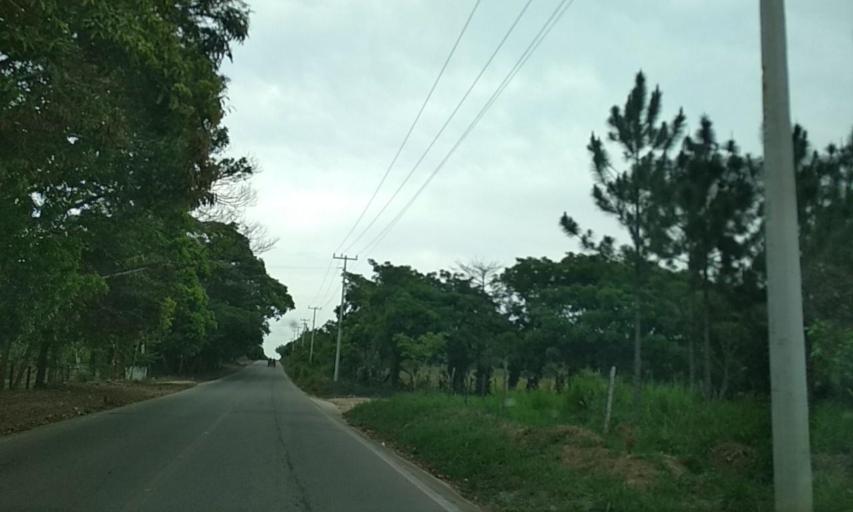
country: MX
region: Veracruz
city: Las Choapas
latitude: 17.8598
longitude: -94.1001
